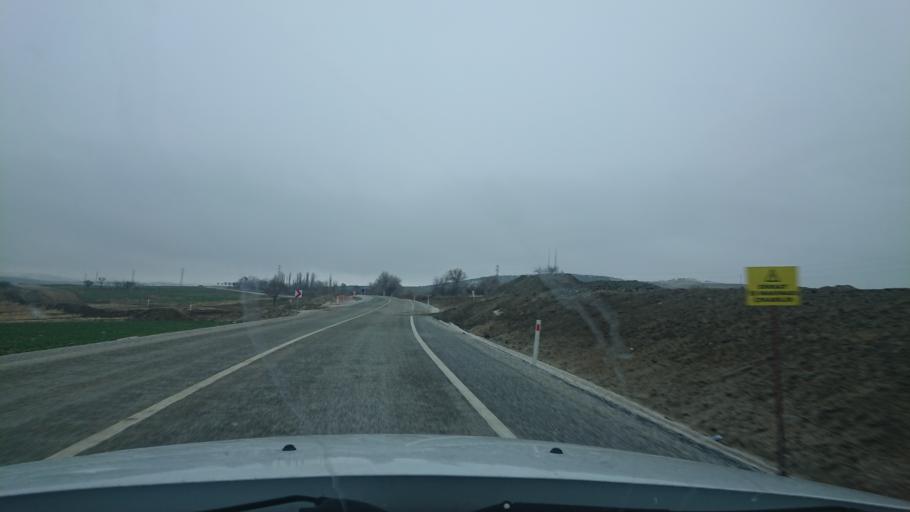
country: TR
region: Aksaray
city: Agacoren
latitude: 38.8909
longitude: 33.9287
